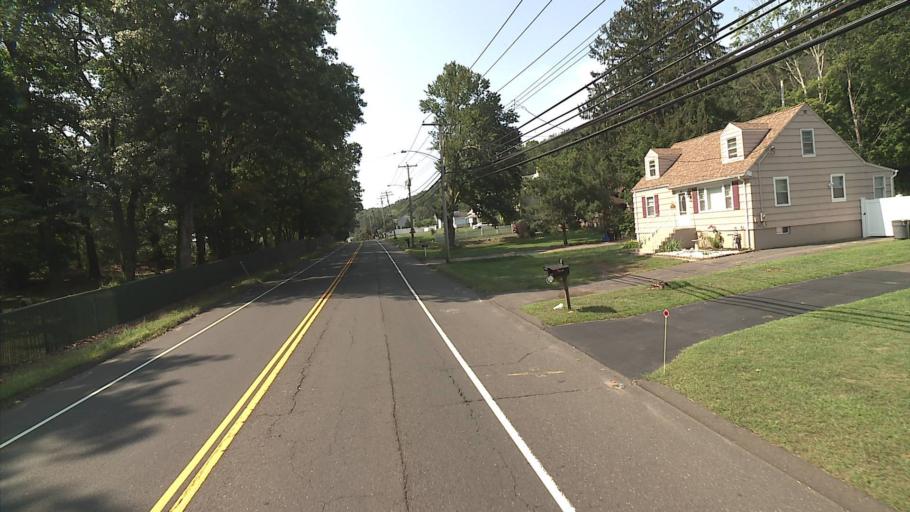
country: US
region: Connecticut
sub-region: New Haven County
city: East Haven
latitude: 41.2966
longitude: -72.8637
